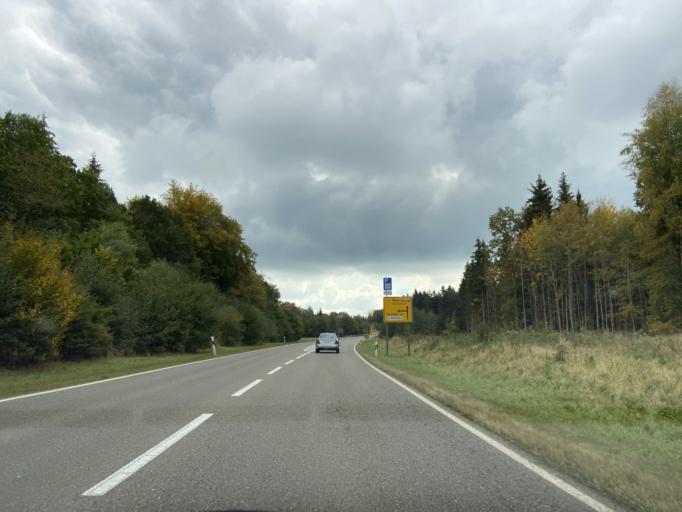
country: DE
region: Baden-Wuerttemberg
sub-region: Tuebingen Region
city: Sigmaringen
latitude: 48.0675
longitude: 9.2235
